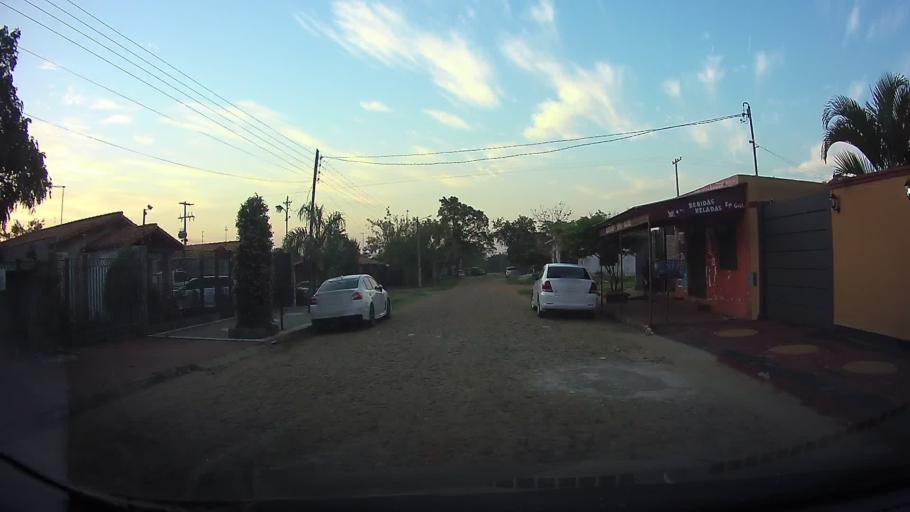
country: PY
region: Central
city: Limpio
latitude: -25.2334
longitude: -57.4687
